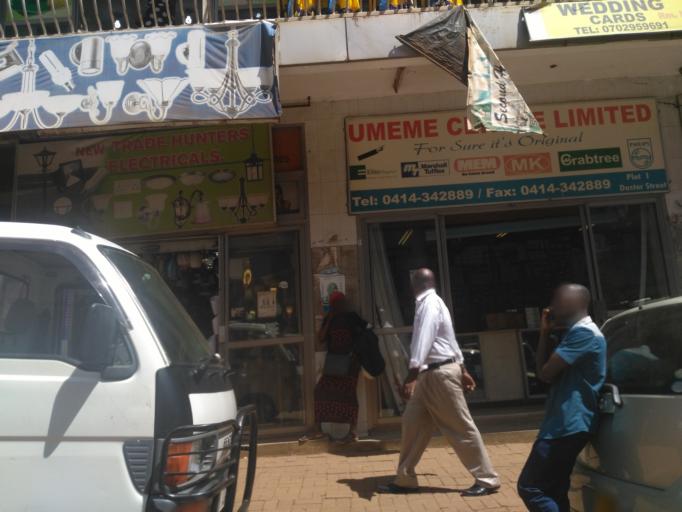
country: UG
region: Central Region
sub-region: Kampala District
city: Kampala
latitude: 0.3126
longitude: 32.5796
